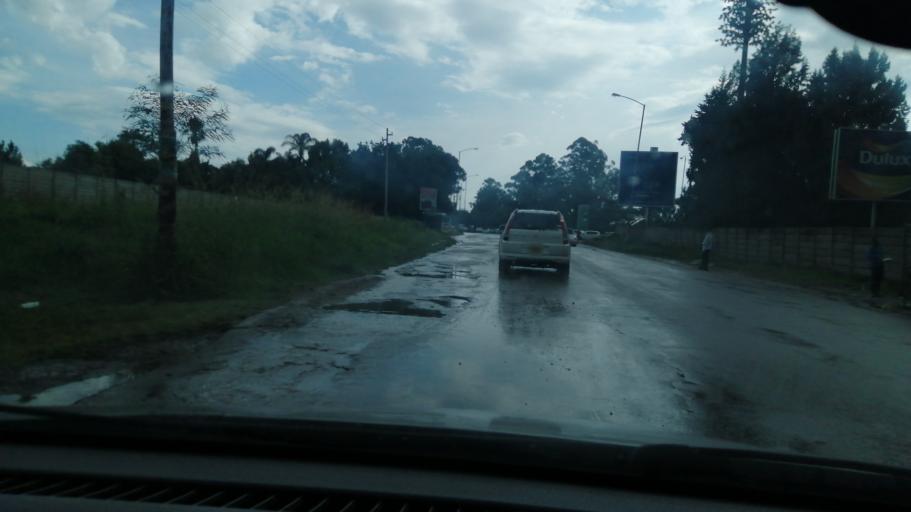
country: ZW
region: Harare
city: Harare
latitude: -17.7758
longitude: 31.0670
